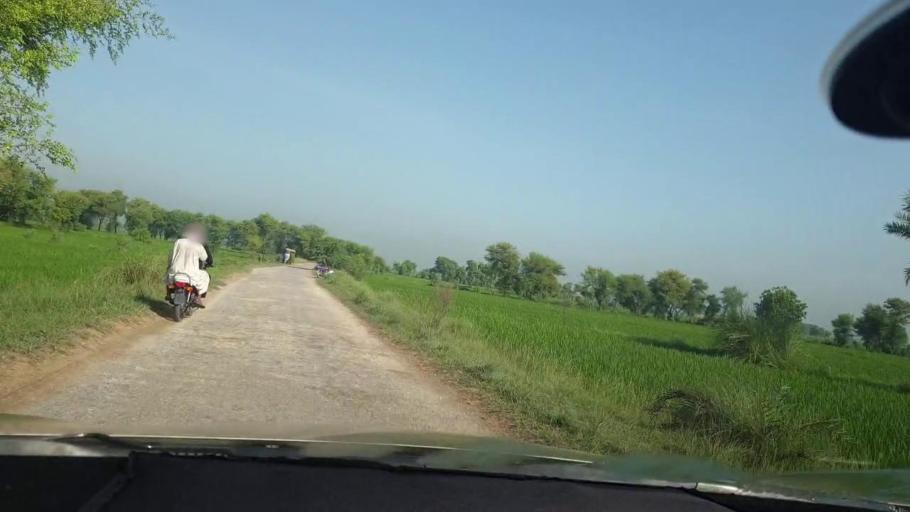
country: PK
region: Sindh
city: Kambar
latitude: 27.6593
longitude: 68.0231
